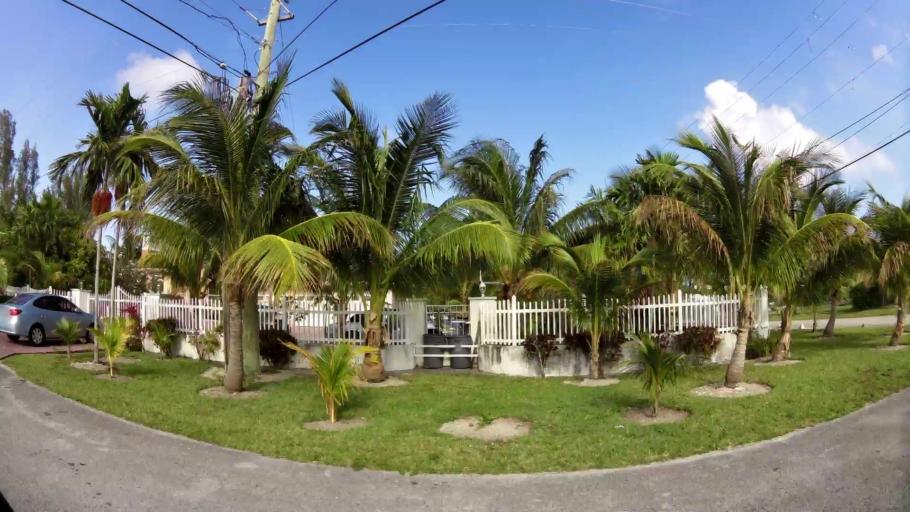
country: BS
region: Freeport
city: Lucaya
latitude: 26.5037
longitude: -78.6603
